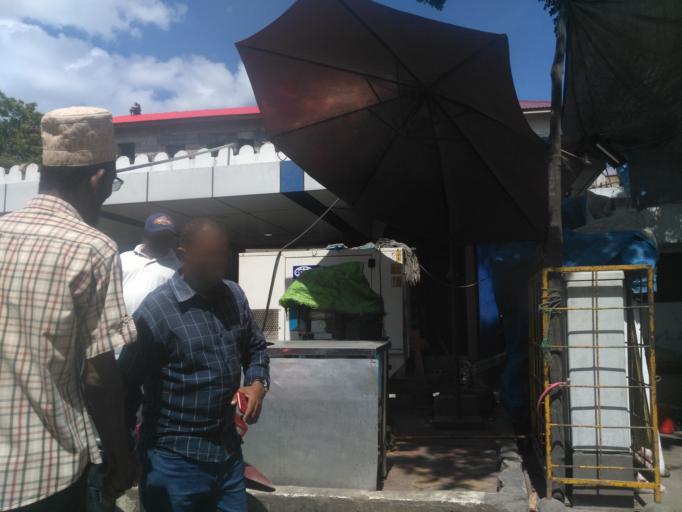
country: TZ
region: Zanzibar Urban/West
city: Zanzibar
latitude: -6.1570
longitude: 39.1941
